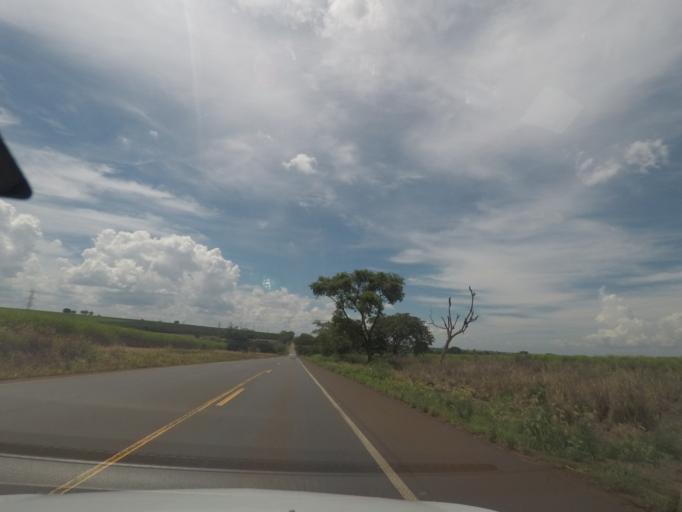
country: BR
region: Sao Paulo
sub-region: Barretos
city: Barretos
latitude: -20.2649
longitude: -48.6741
